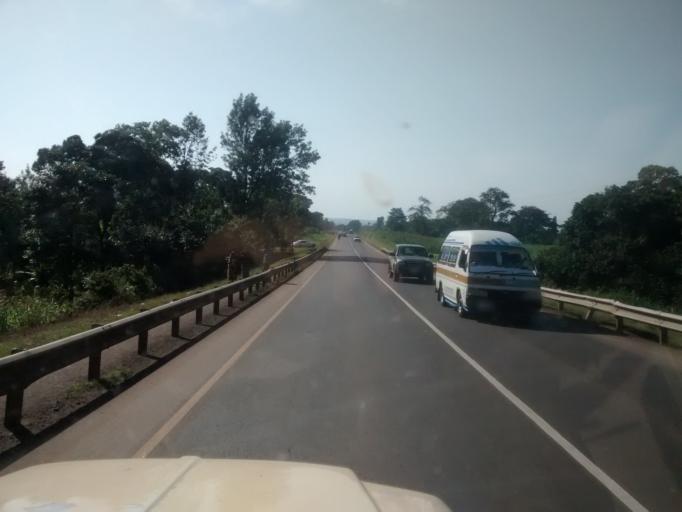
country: TZ
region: Arusha
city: Nkoaranga
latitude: -3.3711
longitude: 36.8017
